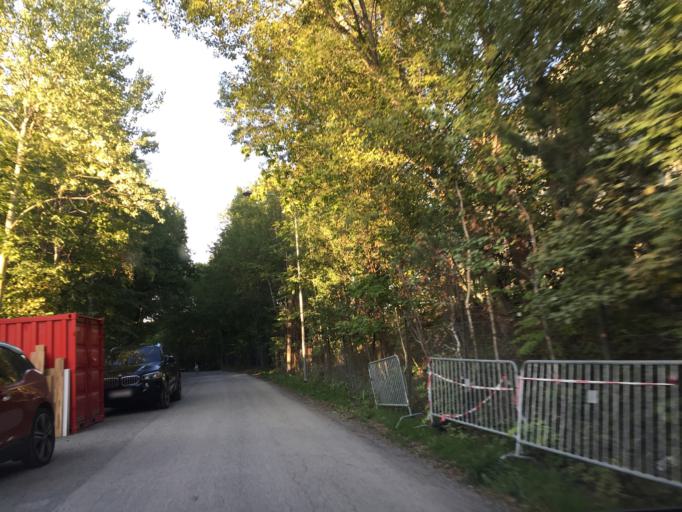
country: NO
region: Akershus
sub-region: Baerum
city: Lysaker
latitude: 59.9010
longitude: 10.6123
